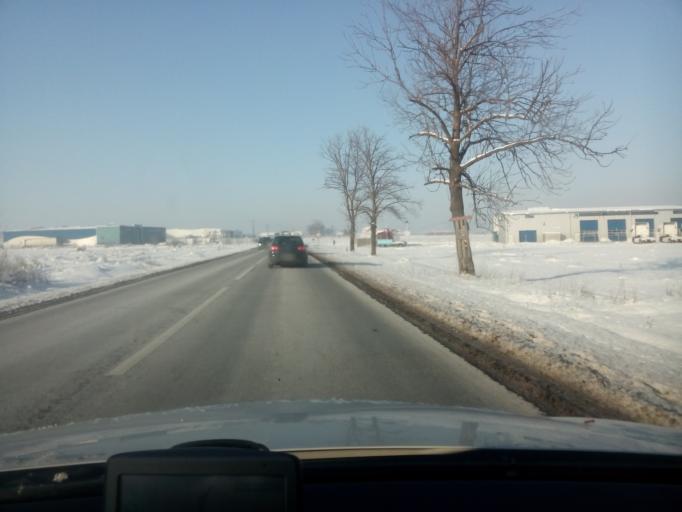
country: RO
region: Sibiu
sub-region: Comuna Talmaciu
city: Talmaciu
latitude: 45.6807
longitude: 24.2591
